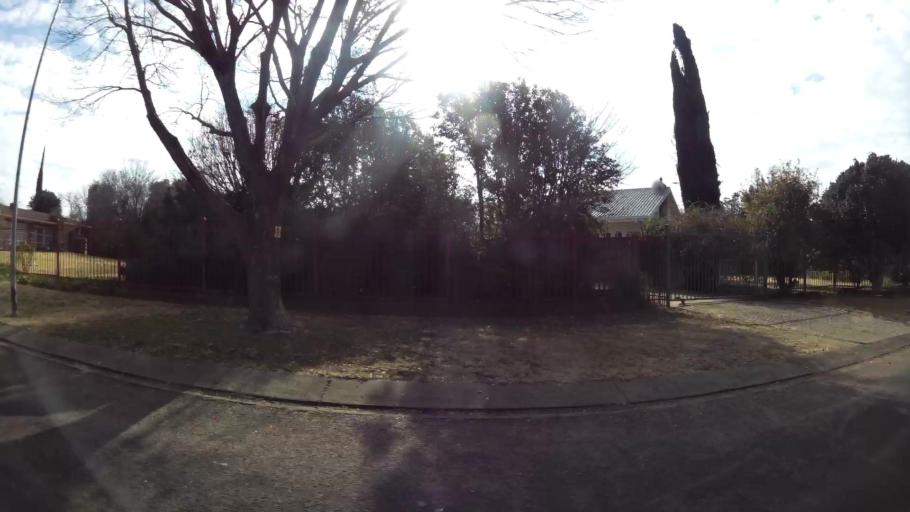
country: ZA
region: Orange Free State
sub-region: Mangaung Metropolitan Municipality
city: Bloemfontein
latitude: -29.0762
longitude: 26.2399
